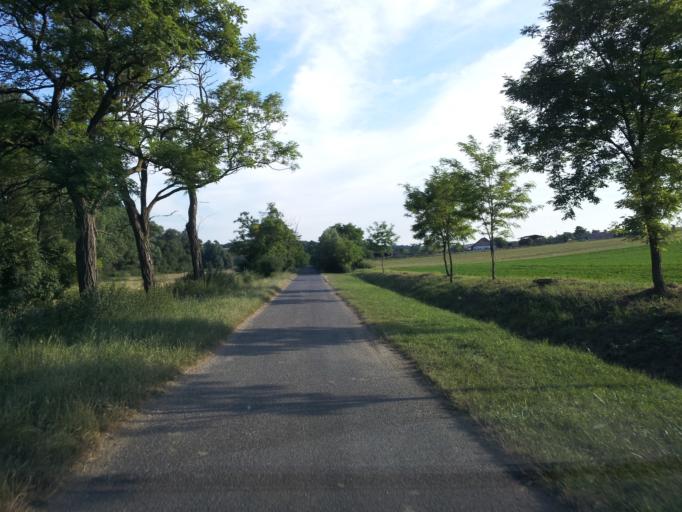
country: HU
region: Fejer
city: Many
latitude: 47.5637
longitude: 18.5977
